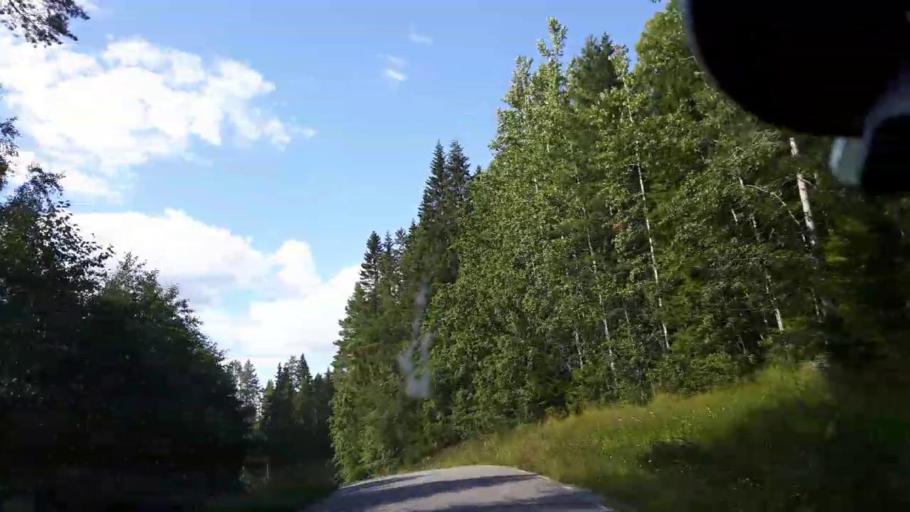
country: SE
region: Jaemtland
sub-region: Braecke Kommun
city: Braecke
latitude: 62.8619
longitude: 15.2757
